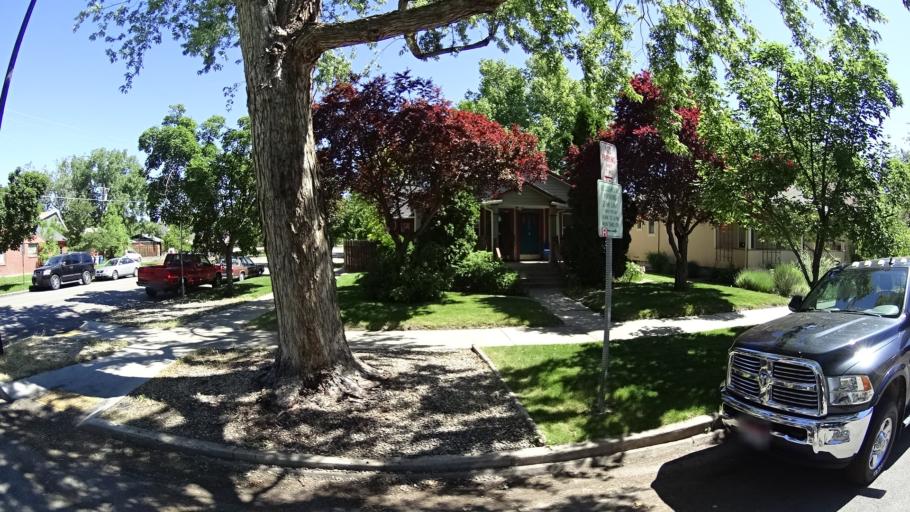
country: US
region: Idaho
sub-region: Ada County
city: Boise
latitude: 43.6237
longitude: -116.2128
